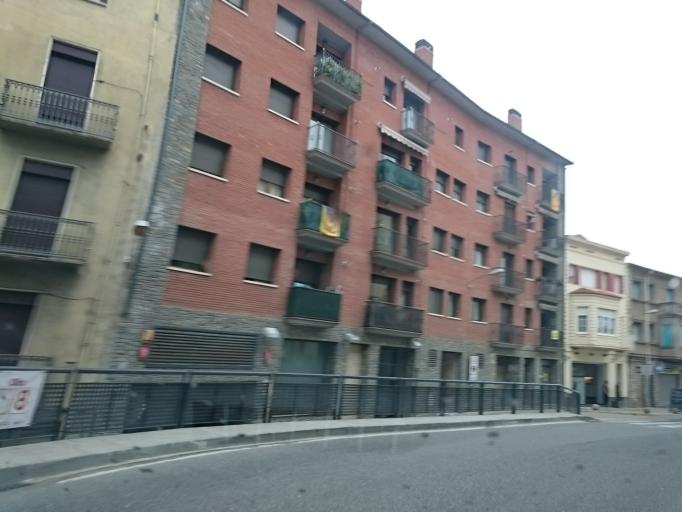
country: ES
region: Catalonia
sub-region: Provincia de Lleida
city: Senterada
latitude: 42.2471
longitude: 0.9684
